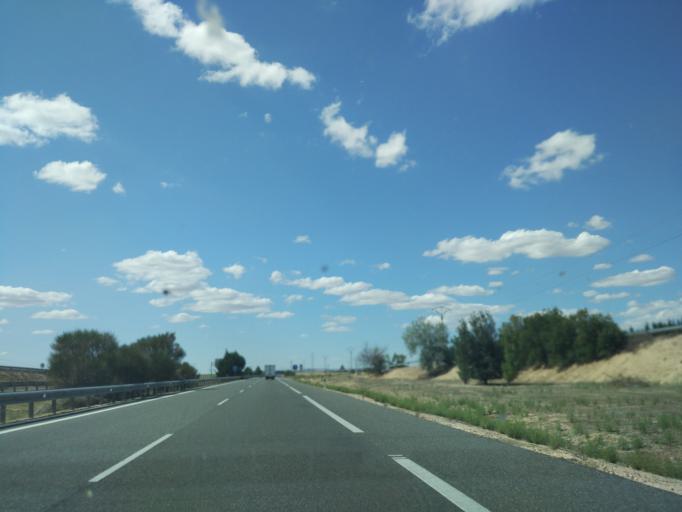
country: ES
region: Castille and Leon
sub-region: Provincia de Valladolid
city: San Vicente del Palacio
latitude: 41.2221
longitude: -4.8441
